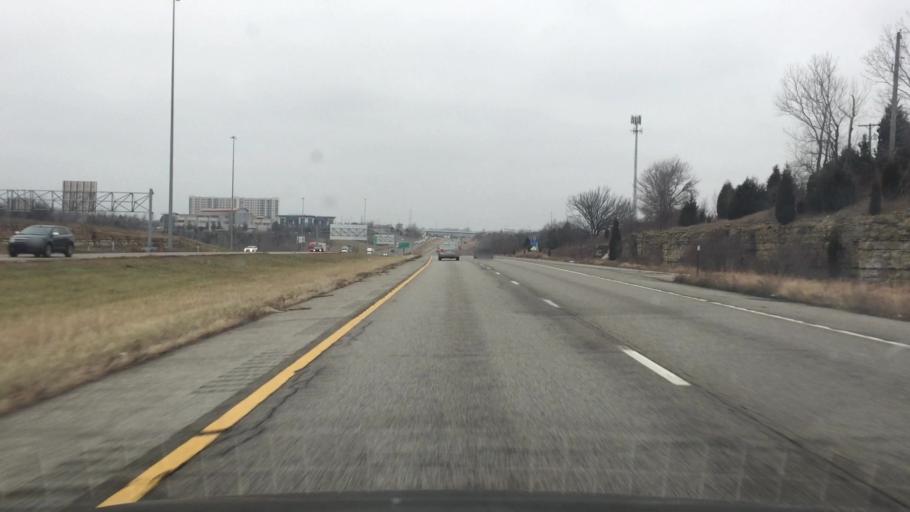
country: US
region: Kansas
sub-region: Johnson County
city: Lenexa
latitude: 38.9421
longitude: -94.7845
